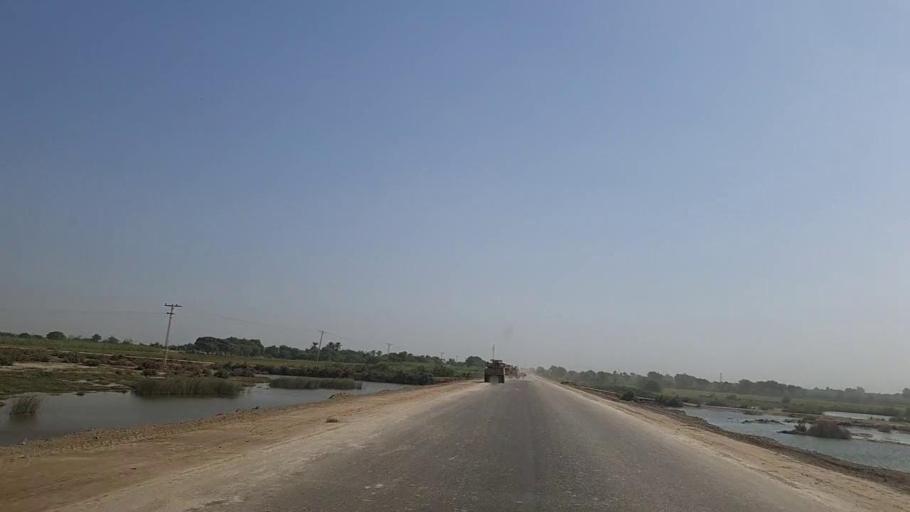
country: PK
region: Sindh
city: Mirpur Batoro
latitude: 24.7466
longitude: 68.2411
